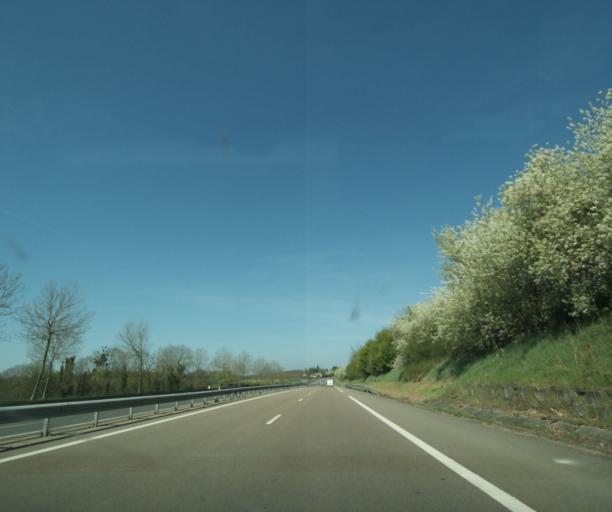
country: FR
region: Bourgogne
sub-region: Departement de la Nievre
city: Pougues-les-Eaux
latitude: 47.0996
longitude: 3.0768
